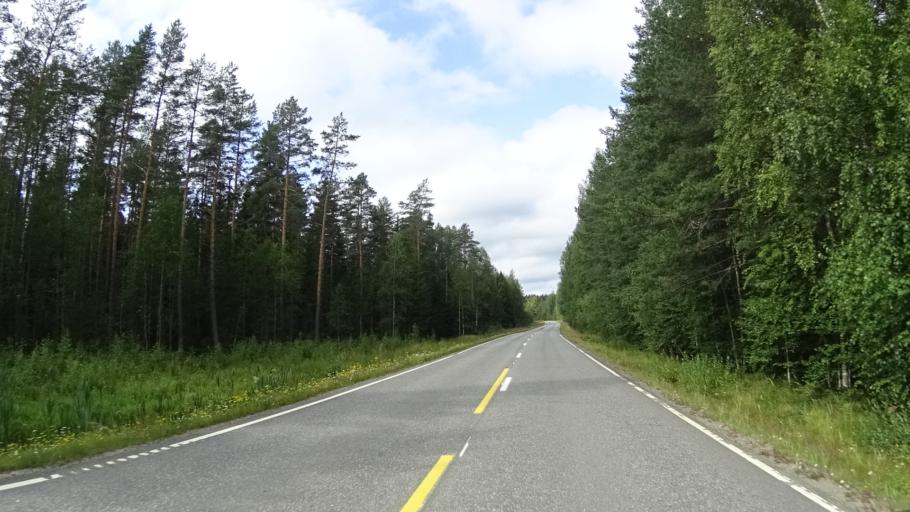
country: FI
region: Pirkanmaa
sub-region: Tampere
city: Luopioinen
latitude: 61.4965
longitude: 24.7988
